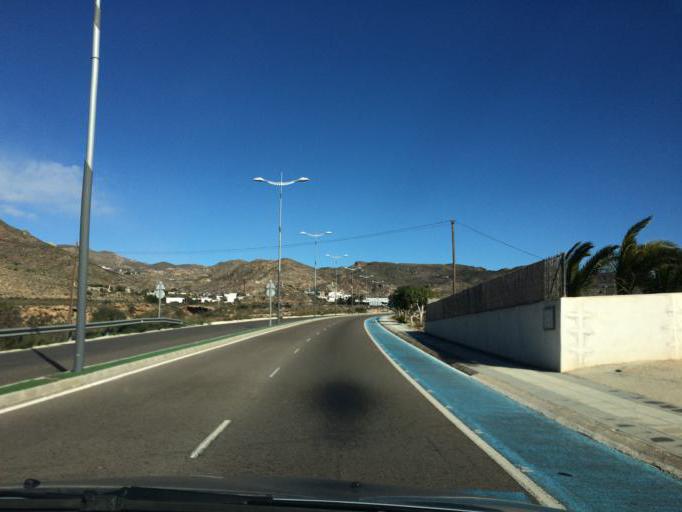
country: ES
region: Andalusia
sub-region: Provincia de Almeria
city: Nijar
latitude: 36.9529
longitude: -2.2061
